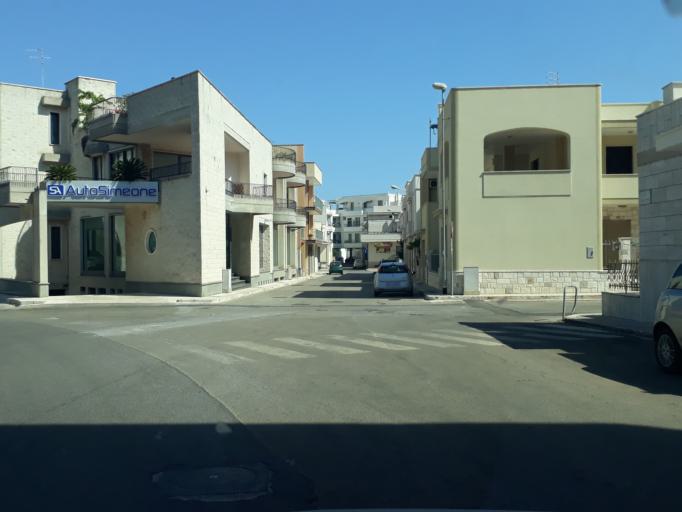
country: IT
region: Apulia
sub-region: Provincia di Brindisi
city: Carovigno
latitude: 40.7125
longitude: 17.6566
